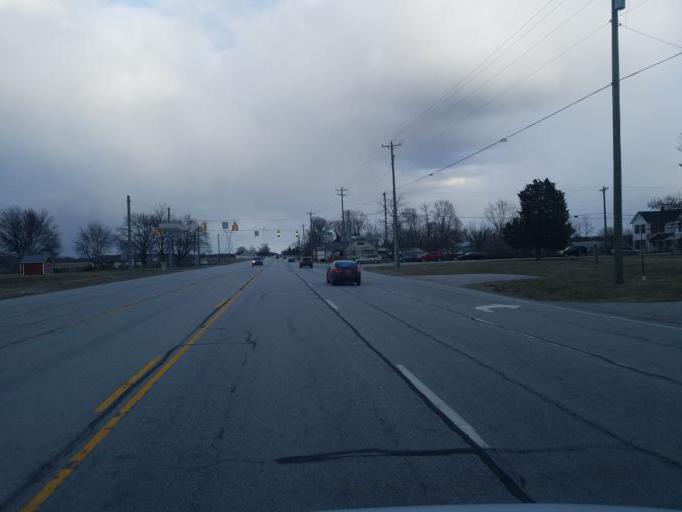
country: US
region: Indiana
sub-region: Hancock County
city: New Palestine
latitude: 39.7794
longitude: -85.8977
